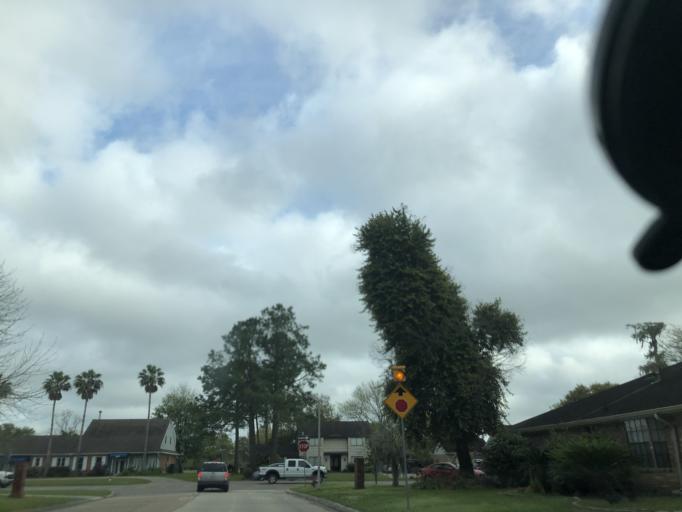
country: US
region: Louisiana
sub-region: Saint Charles Parish
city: New Sarpy
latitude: 29.9690
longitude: -90.3702
